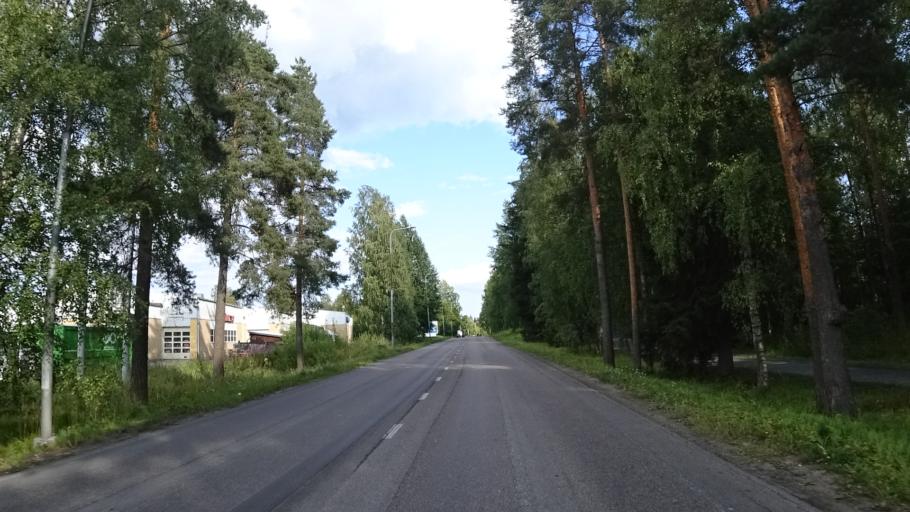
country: FI
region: South Karelia
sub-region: Imatra
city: Imatra
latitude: 61.1714
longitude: 28.7540
